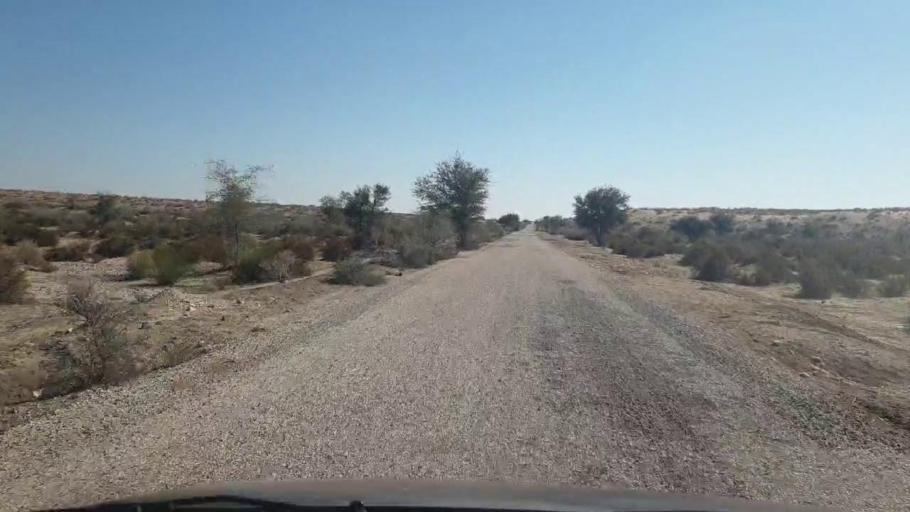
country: PK
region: Sindh
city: Bozdar
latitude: 27.0389
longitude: 68.6921
